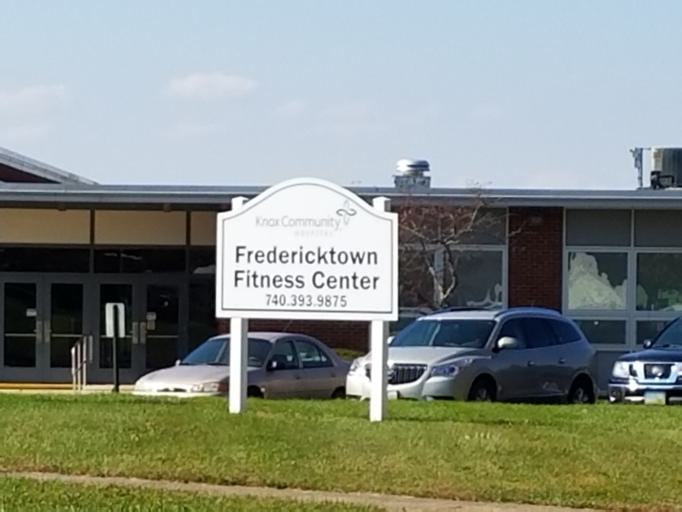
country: US
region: Ohio
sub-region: Knox County
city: Fredericktown
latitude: 40.4768
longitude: -82.5443
